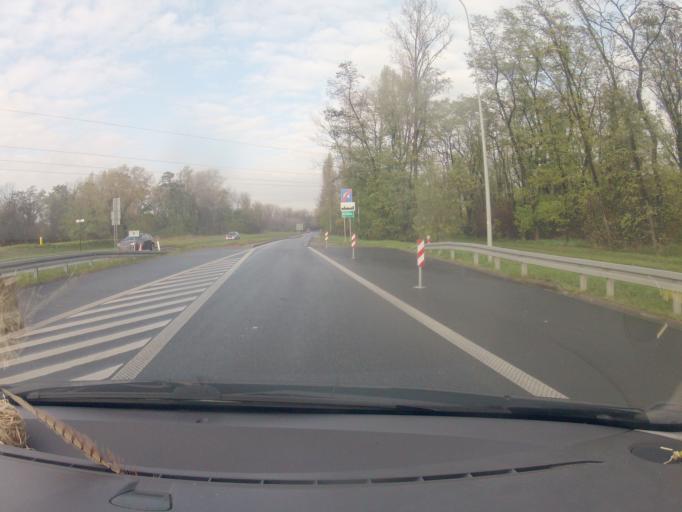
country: PL
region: Lesser Poland Voivodeship
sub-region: Powiat wielicki
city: Kokotow
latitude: 50.0703
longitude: 20.0669
